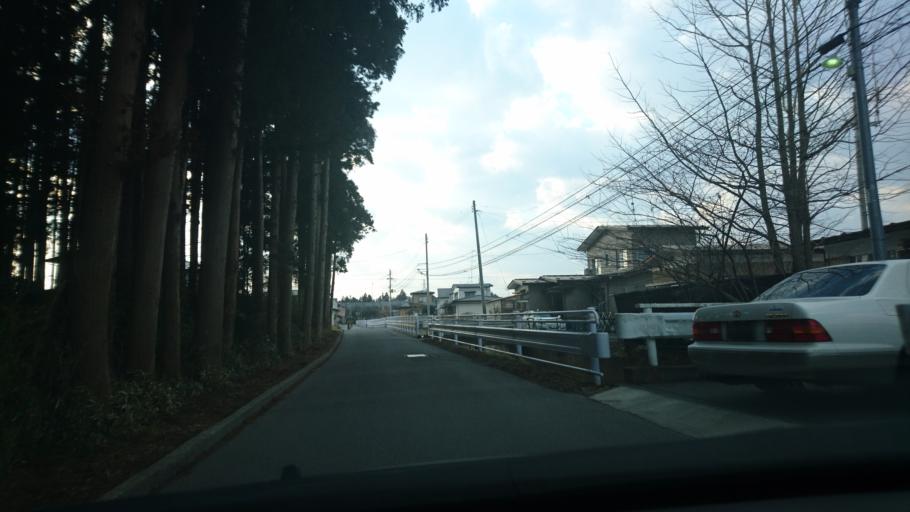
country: JP
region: Iwate
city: Ichinoseki
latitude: 38.9360
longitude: 141.1044
